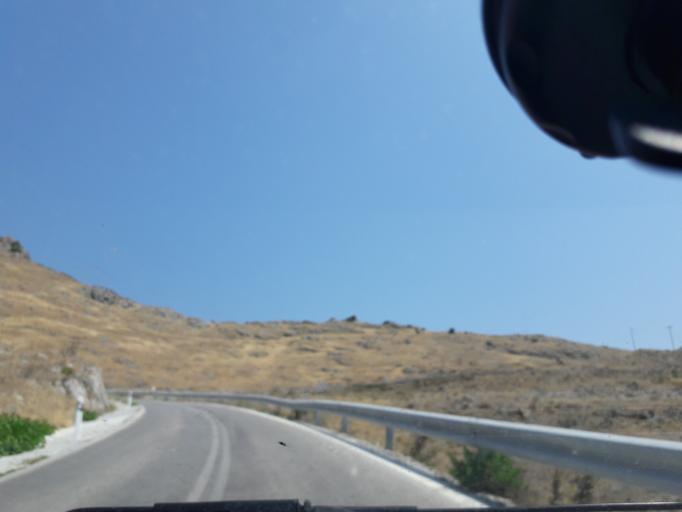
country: GR
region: North Aegean
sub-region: Nomos Lesvou
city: Myrina
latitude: 39.8633
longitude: 25.0769
